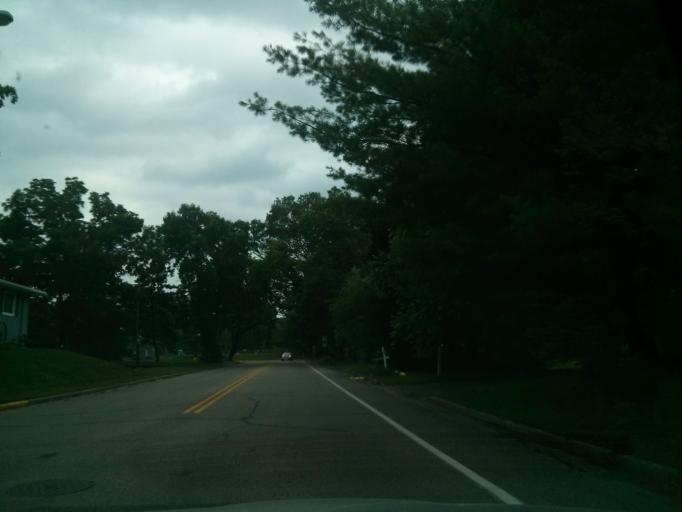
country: US
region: Wisconsin
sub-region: Saint Croix County
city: Hudson
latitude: 44.9717
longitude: -92.7437
